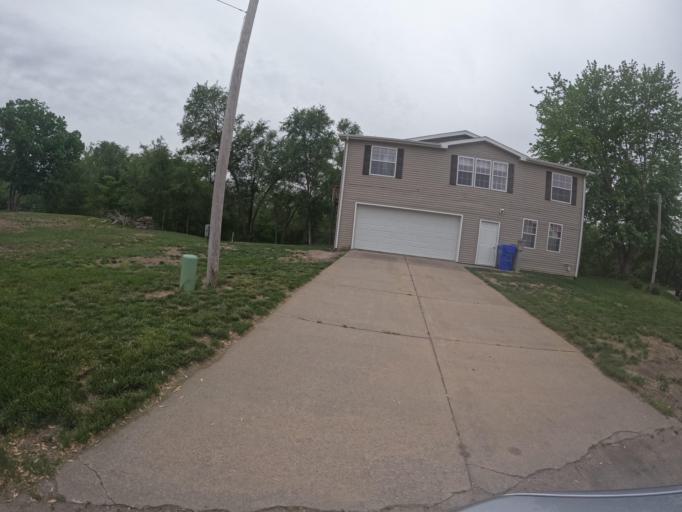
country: US
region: Nebraska
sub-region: Sarpy County
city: Offutt Air Force Base
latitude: 41.0529
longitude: -95.9566
